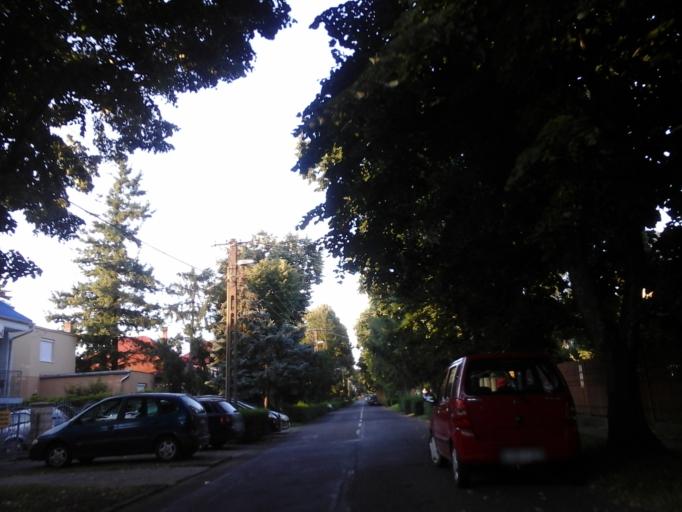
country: HU
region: Hajdu-Bihar
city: Hajduszoboszlo
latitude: 47.4563
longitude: 21.4058
